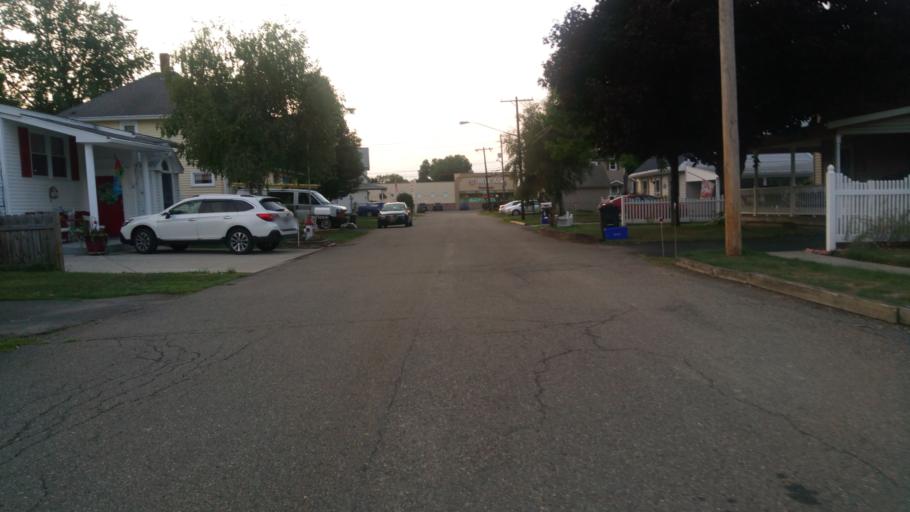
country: US
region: New York
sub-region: Chemung County
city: Southport
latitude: 42.0592
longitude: -76.8108
